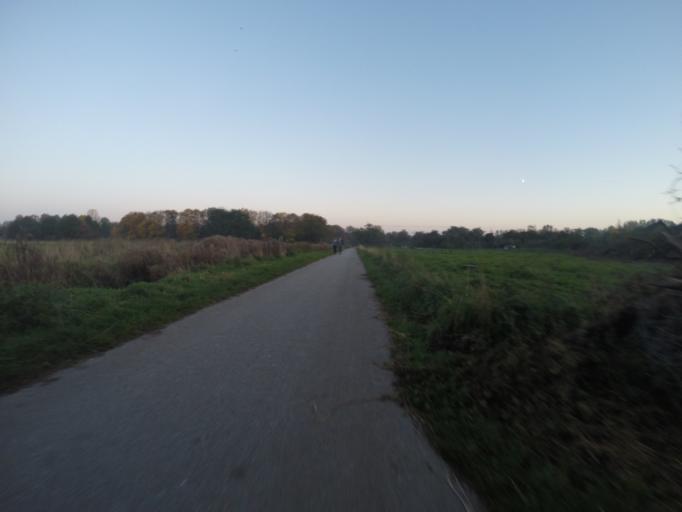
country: DK
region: Capital Region
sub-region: Hoje-Taastrup Kommune
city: Taastrup
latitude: 55.6576
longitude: 12.3255
